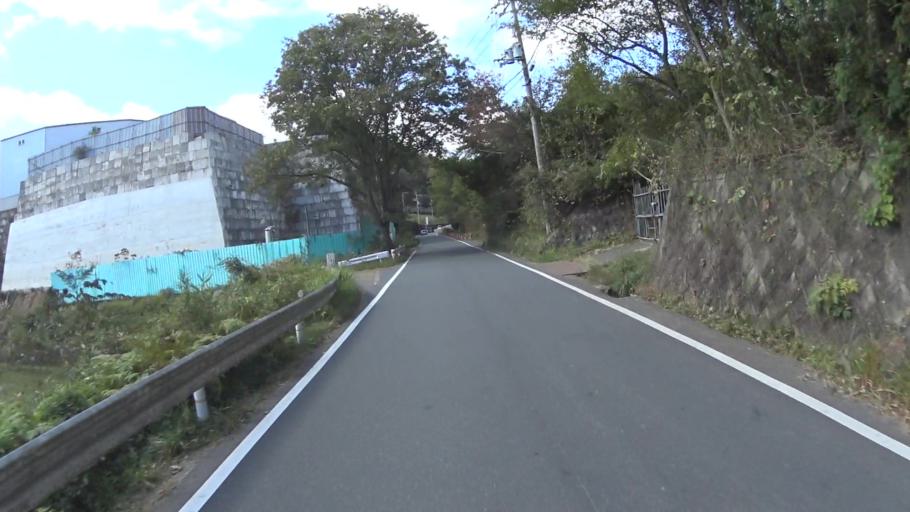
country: JP
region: Kyoto
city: Kameoka
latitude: 35.1632
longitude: 135.4635
